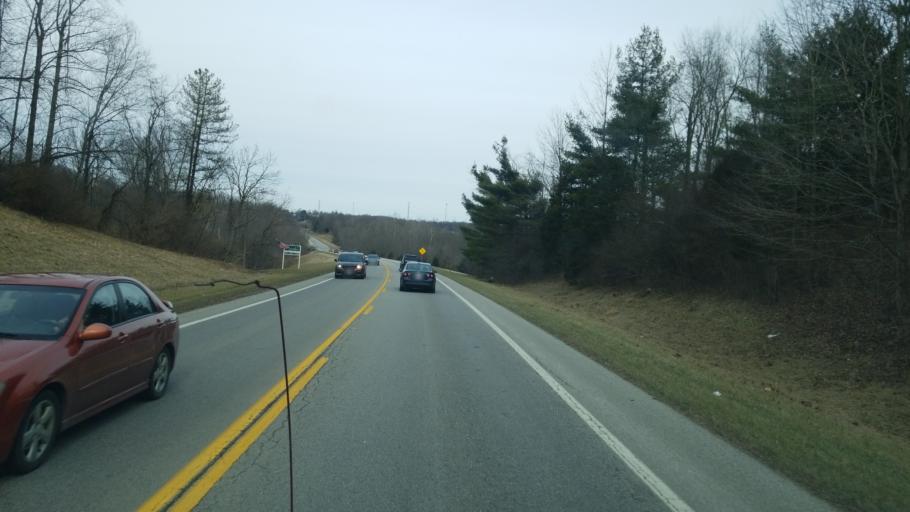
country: US
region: Ohio
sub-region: Highland County
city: Hillsboro
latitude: 39.1720
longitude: -83.6240
